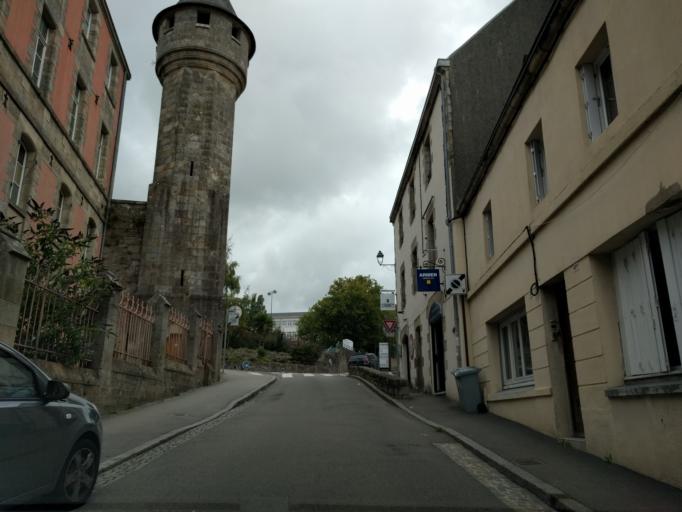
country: FR
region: Brittany
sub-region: Departement du Finistere
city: Quimper
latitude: 47.9984
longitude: -4.1023
